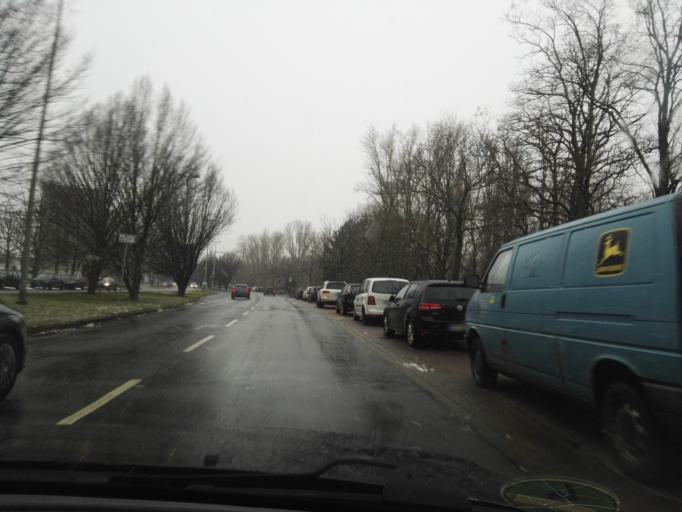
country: DE
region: Lower Saxony
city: Braunschweig
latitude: 52.2513
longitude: 10.5189
